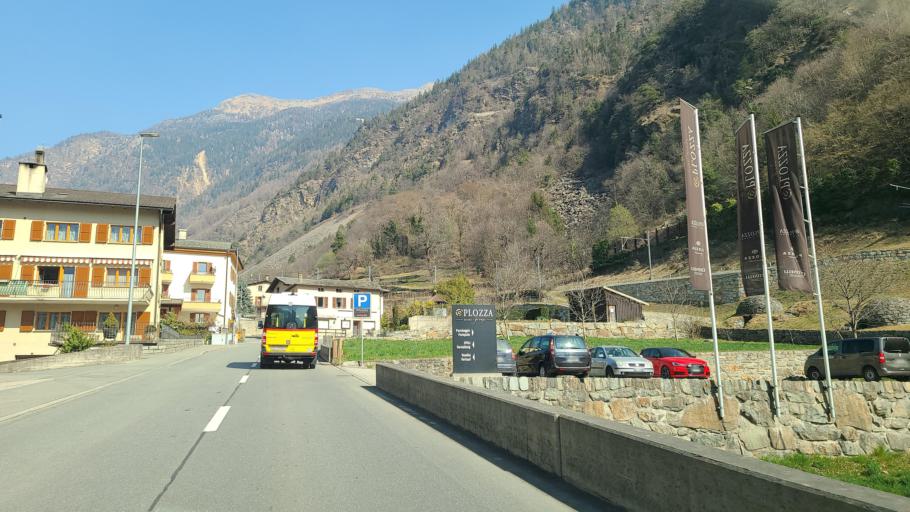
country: CH
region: Grisons
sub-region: Bernina District
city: Brusio
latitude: 46.2565
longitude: 10.1278
